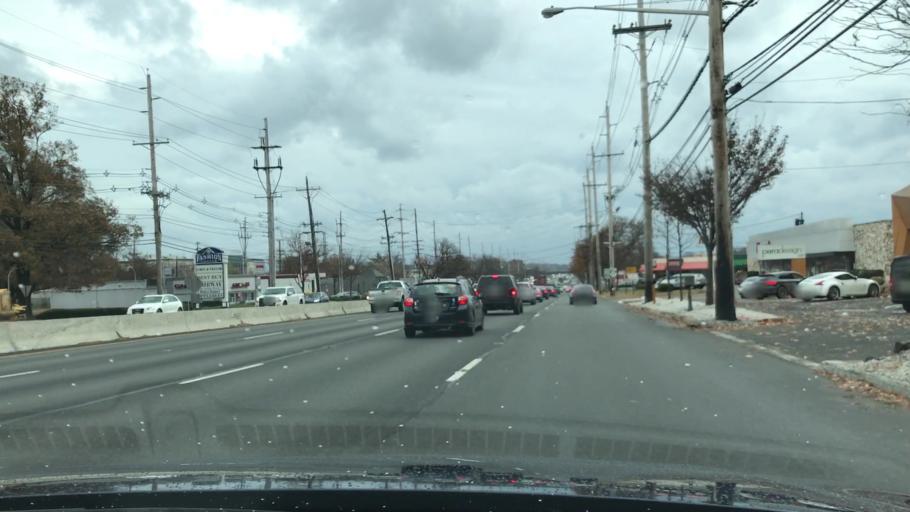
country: US
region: New Jersey
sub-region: Bergen County
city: Paramus
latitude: 40.9681
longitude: -74.0789
